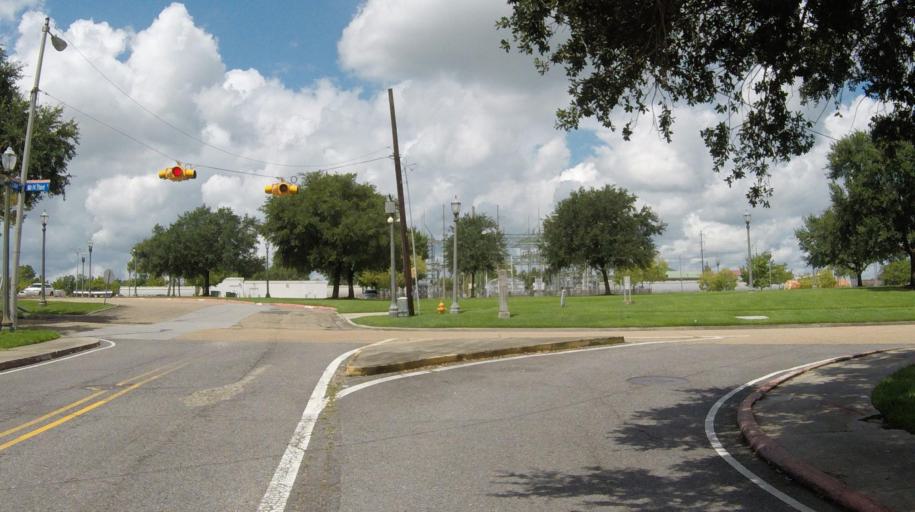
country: US
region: Louisiana
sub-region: West Baton Rouge Parish
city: Port Allen
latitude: 30.4581
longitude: -91.1881
